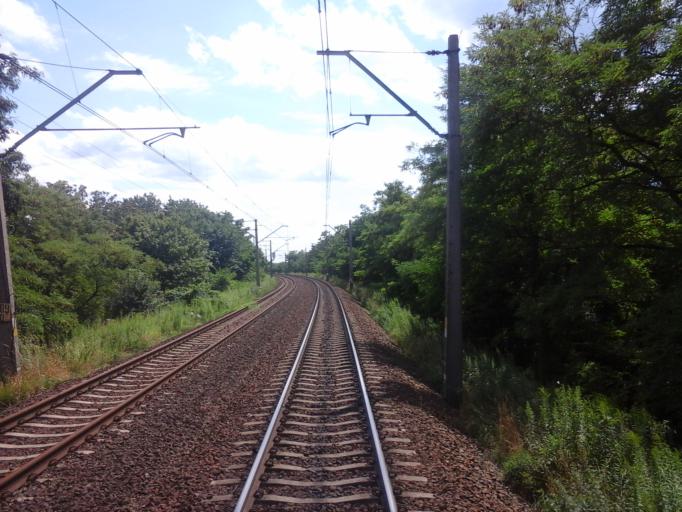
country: PL
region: West Pomeranian Voivodeship
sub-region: Szczecin
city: Szczecin
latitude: 53.3874
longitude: 14.5269
